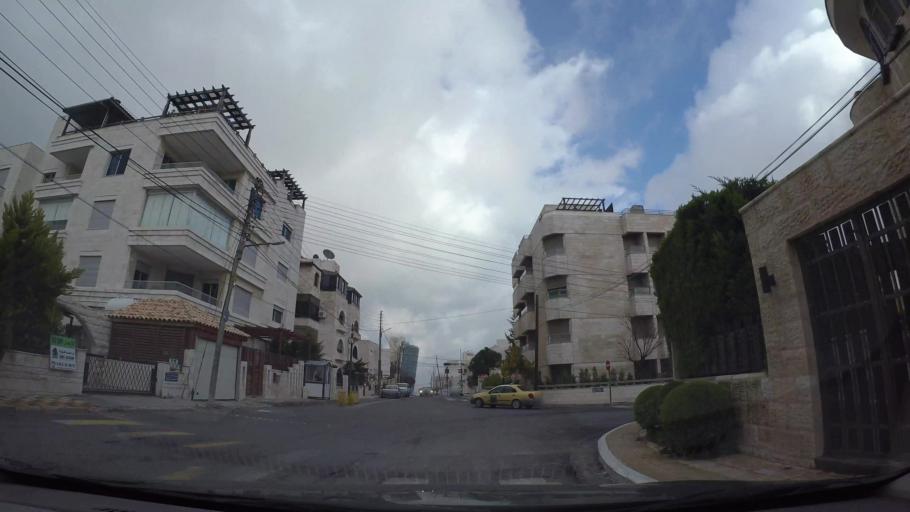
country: JO
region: Amman
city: Wadi as Sir
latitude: 31.9572
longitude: 35.8748
